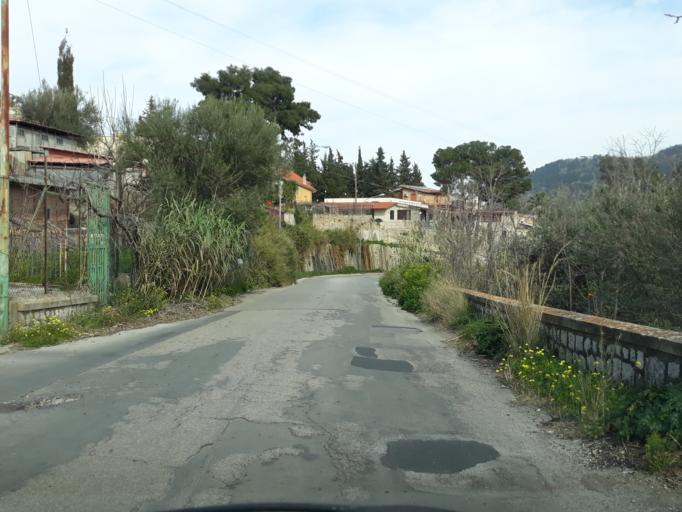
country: IT
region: Sicily
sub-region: Palermo
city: Piano Maglio-Blandino
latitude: 38.0667
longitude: 13.3044
